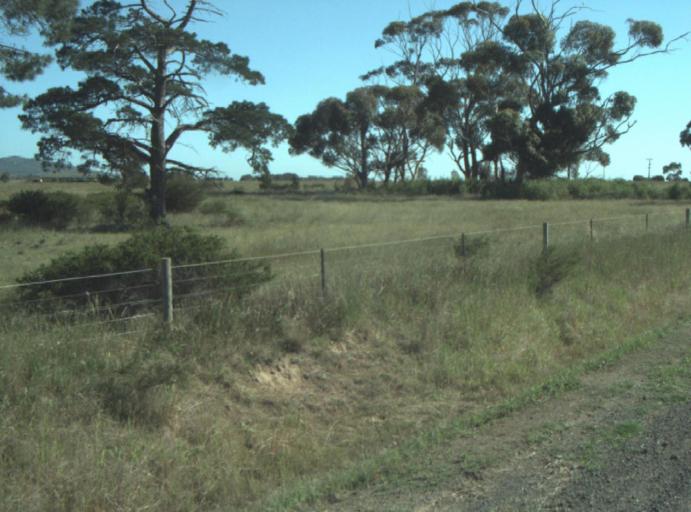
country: AU
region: Victoria
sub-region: Wyndham
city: Little River
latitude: -37.9895
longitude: 144.4568
